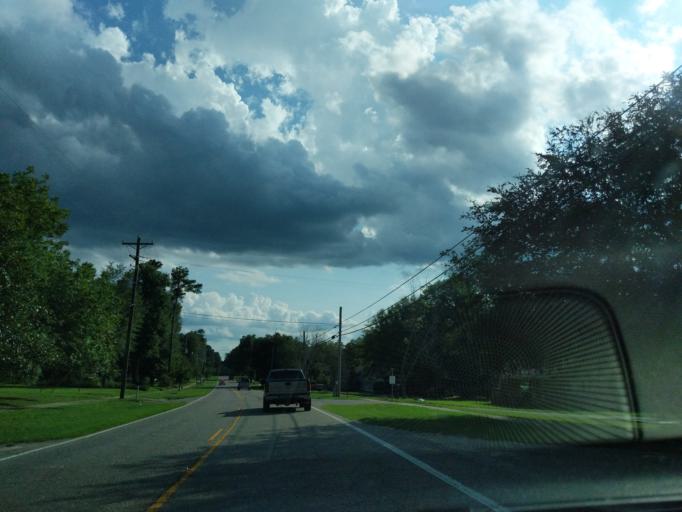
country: US
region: South Carolina
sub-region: Barnwell County
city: Williston
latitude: 33.4097
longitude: -81.4135
